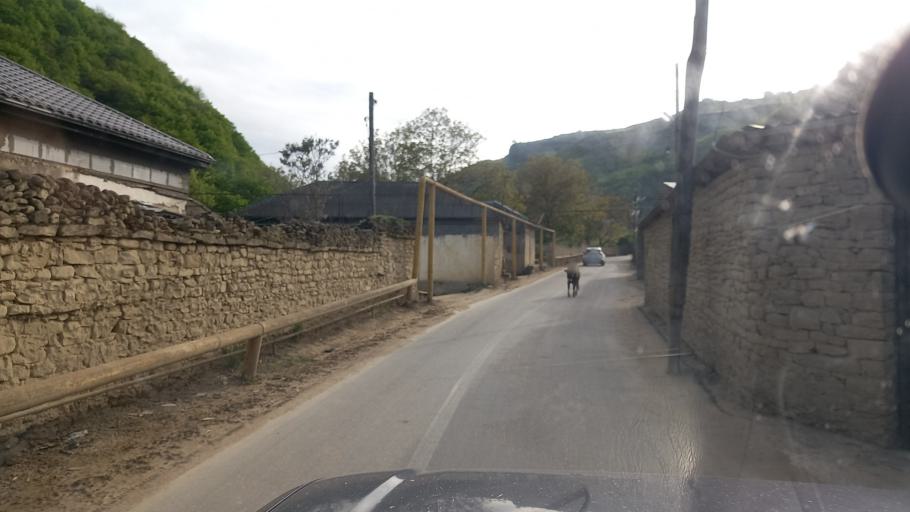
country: RU
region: Dagestan
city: Khuchni
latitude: 41.9721
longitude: 47.8834
